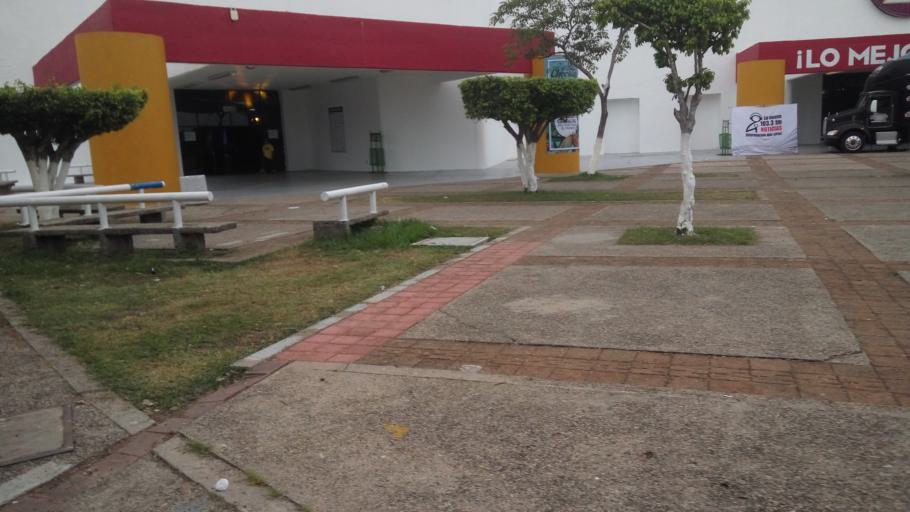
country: MX
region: Tabasco
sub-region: Nacajuca
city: Bosque de Saloya
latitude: 18.0072
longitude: -92.9640
